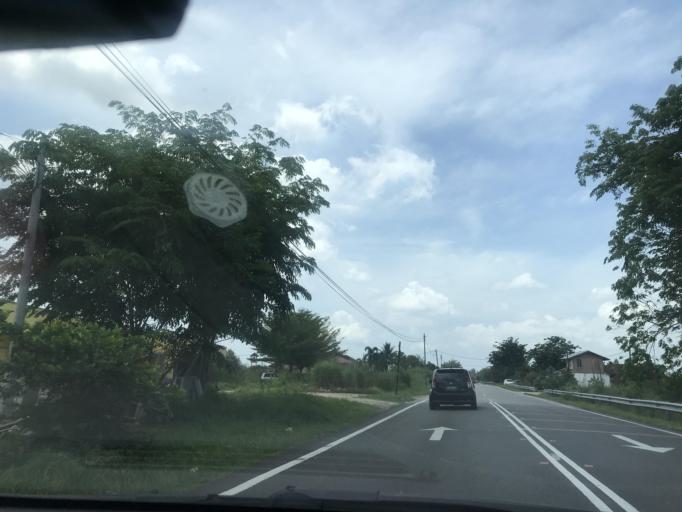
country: MY
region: Kelantan
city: Kota Bharu
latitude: 6.1514
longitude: 102.2090
